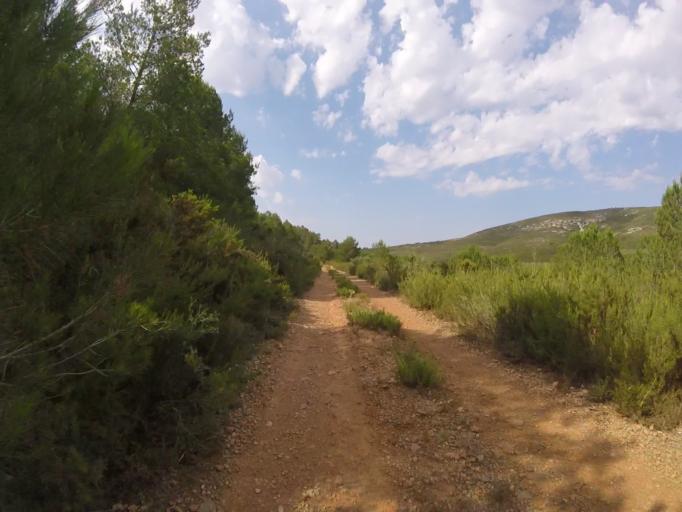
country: ES
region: Valencia
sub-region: Provincia de Castello
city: Alcala de Xivert
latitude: 40.3523
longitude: 0.2000
